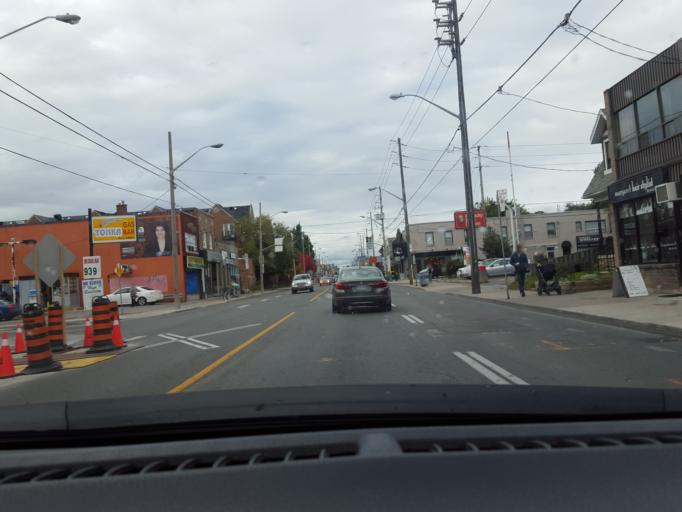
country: CA
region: Ontario
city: Toronto
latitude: 43.6837
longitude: -79.3466
